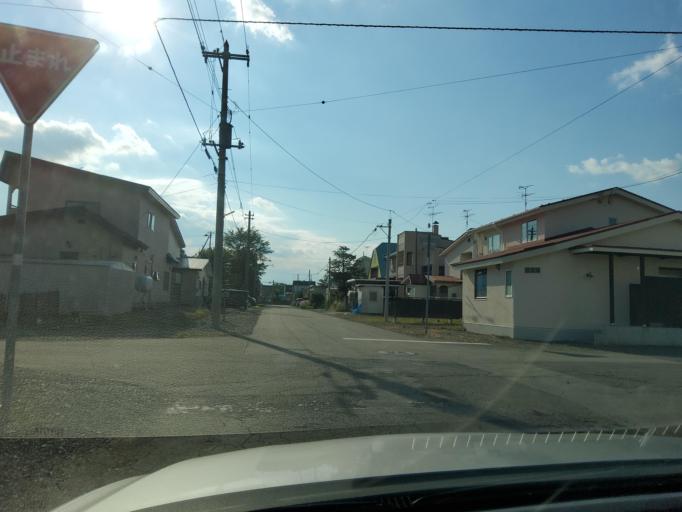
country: JP
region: Hokkaido
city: Obihiro
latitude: 42.8841
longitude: 143.2004
